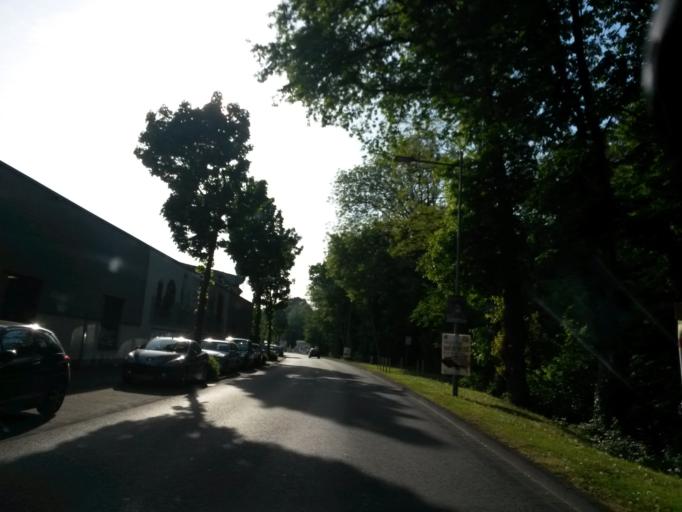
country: DE
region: North Rhine-Westphalia
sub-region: Regierungsbezirk Koln
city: Siegburg
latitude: 50.8018
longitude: 7.1949
